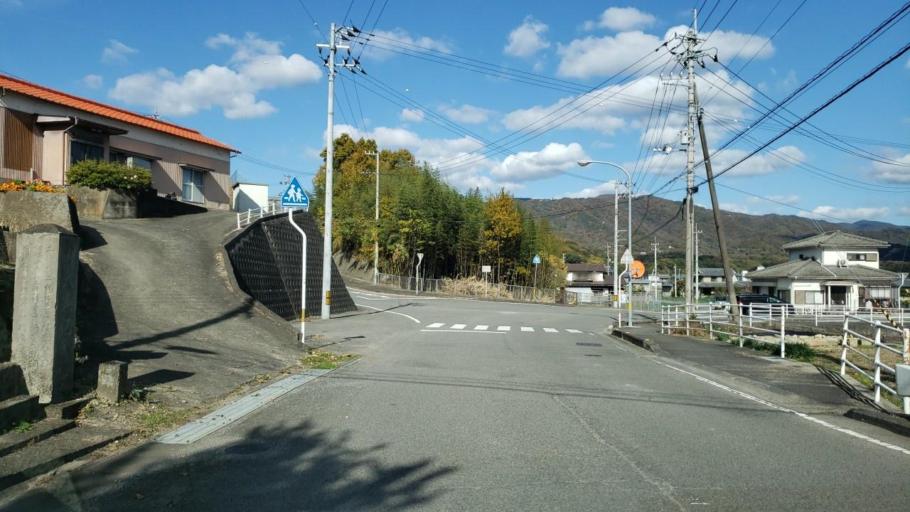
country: JP
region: Tokushima
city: Wakimachi
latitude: 34.0694
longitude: 134.1913
